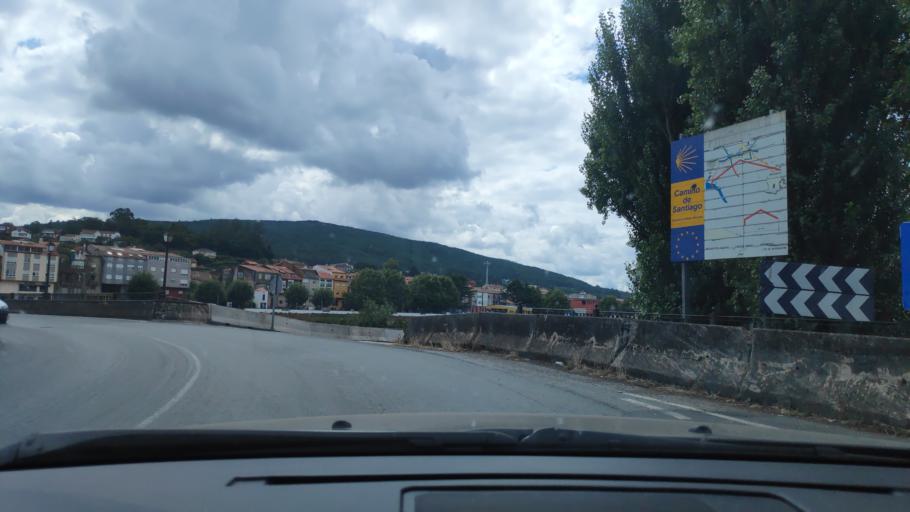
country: ES
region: Galicia
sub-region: Provincia da Coruna
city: Padron
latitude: 42.7255
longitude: -8.6558
